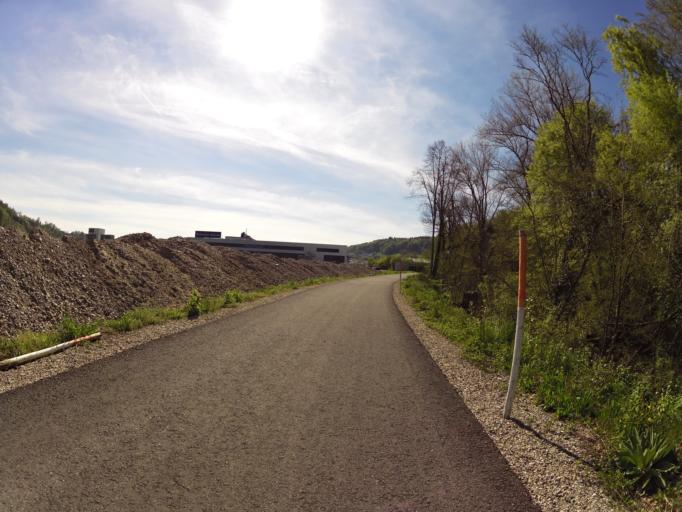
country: CH
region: Solothurn
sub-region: Bezirk Goesgen
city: Niedererlinsbach
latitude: 47.3817
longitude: 8.0141
